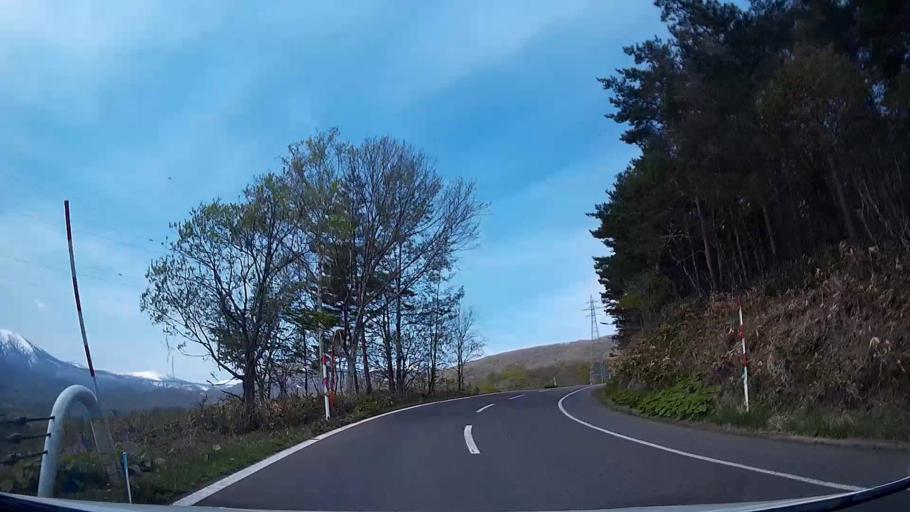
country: JP
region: Iwate
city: Shizukuishi
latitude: 39.9239
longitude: 140.9709
